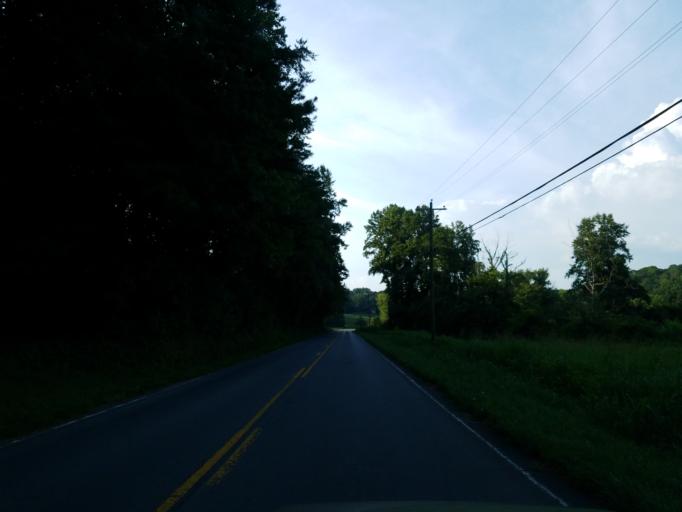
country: US
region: Georgia
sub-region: Gilmer County
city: Ellijay
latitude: 34.6052
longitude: -84.5278
